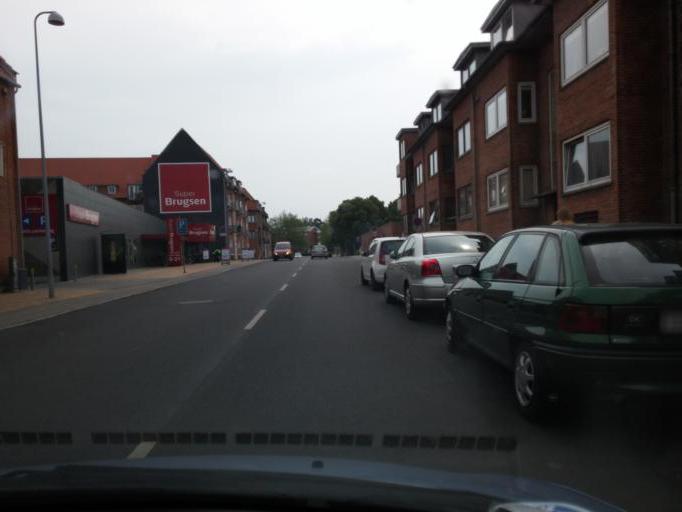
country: DK
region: South Denmark
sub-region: Odense Kommune
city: Odense
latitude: 55.3920
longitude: 10.4068
